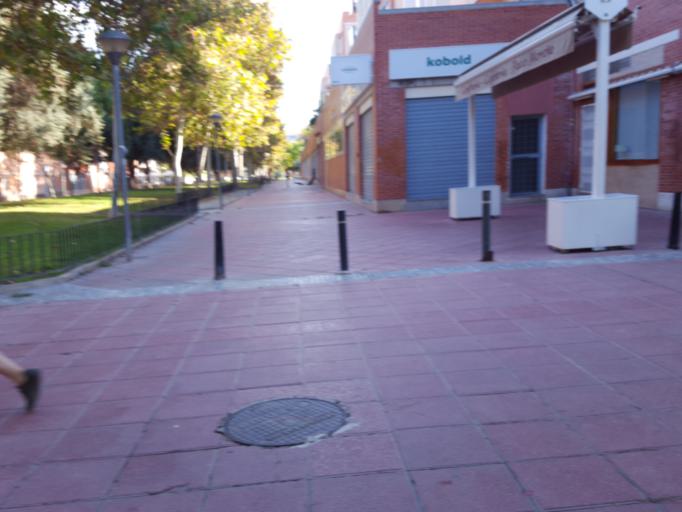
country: ES
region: Murcia
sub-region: Murcia
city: Murcia
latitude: 37.9956
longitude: -1.1244
